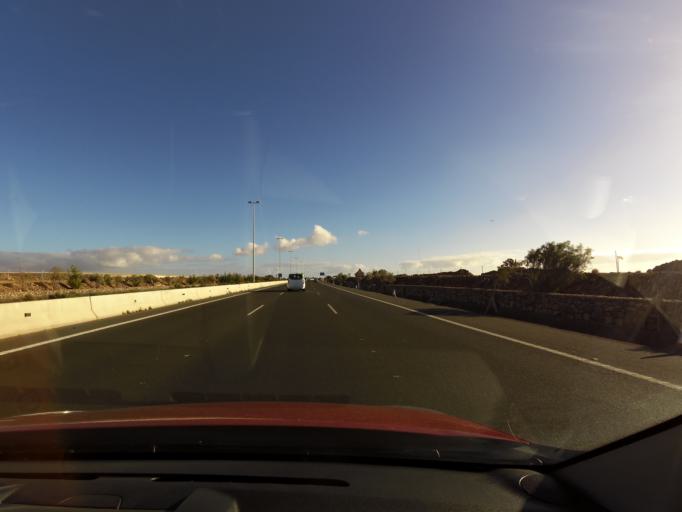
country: ES
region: Canary Islands
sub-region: Provincia de Las Palmas
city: Cruce de Arinaga
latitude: 27.8164
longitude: -15.4709
